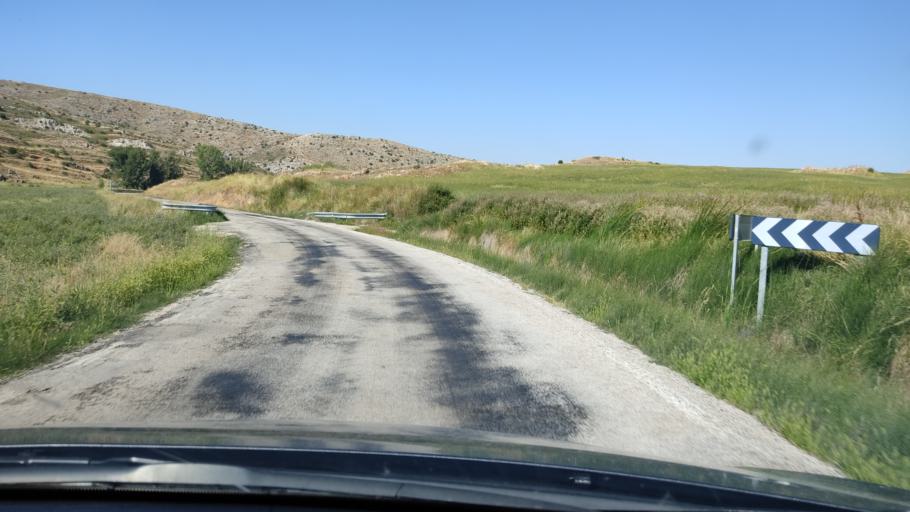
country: ES
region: Aragon
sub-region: Provincia de Teruel
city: Lagueruela
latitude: 41.0412
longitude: -1.1792
